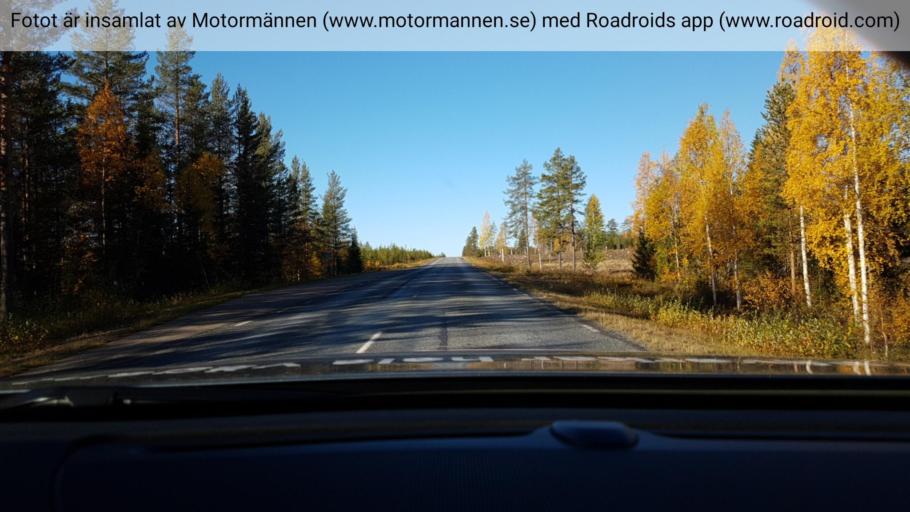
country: SE
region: Vaesterbotten
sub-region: Skelleftea Kommun
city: Boliden
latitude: 65.3826
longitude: 20.1631
